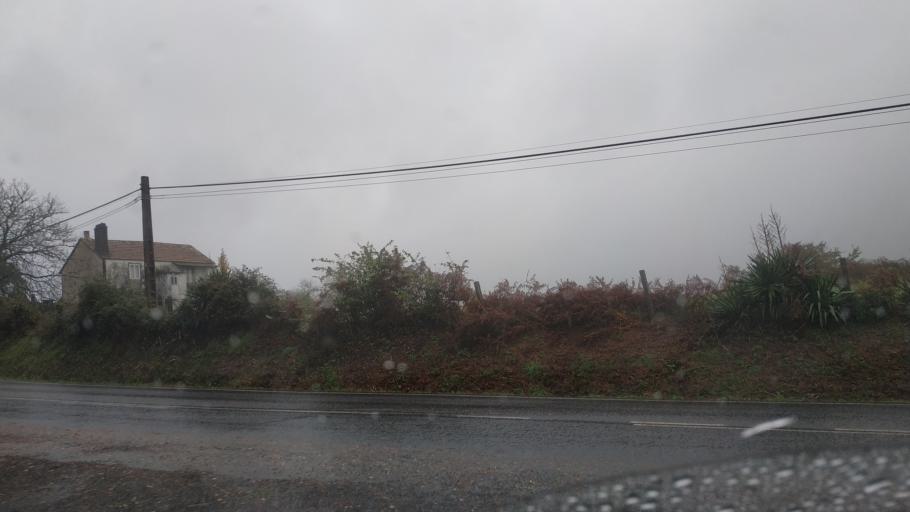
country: ES
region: Galicia
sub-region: Provincia da Coruna
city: Negreira
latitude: 42.9103
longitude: -8.7627
